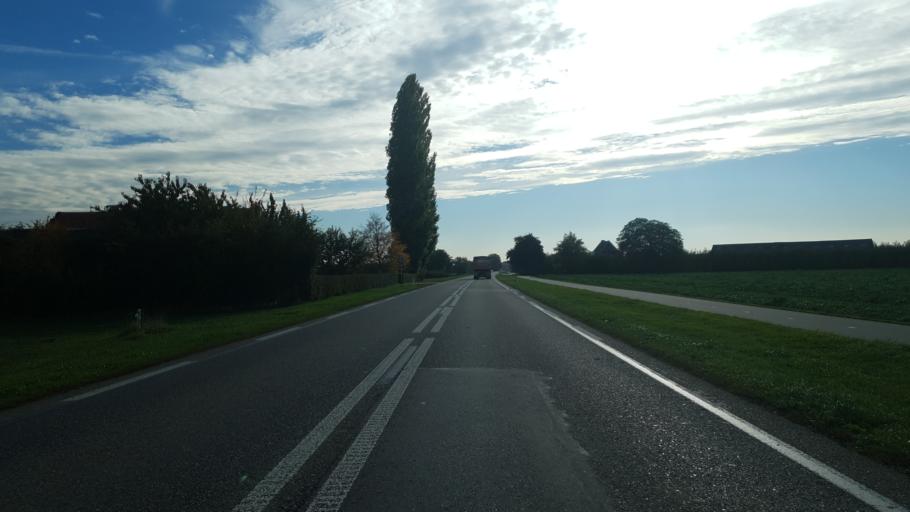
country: DE
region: North Rhine-Westphalia
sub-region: Regierungsbezirk Dusseldorf
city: Kranenburg
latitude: 51.8471
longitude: 6.0049
